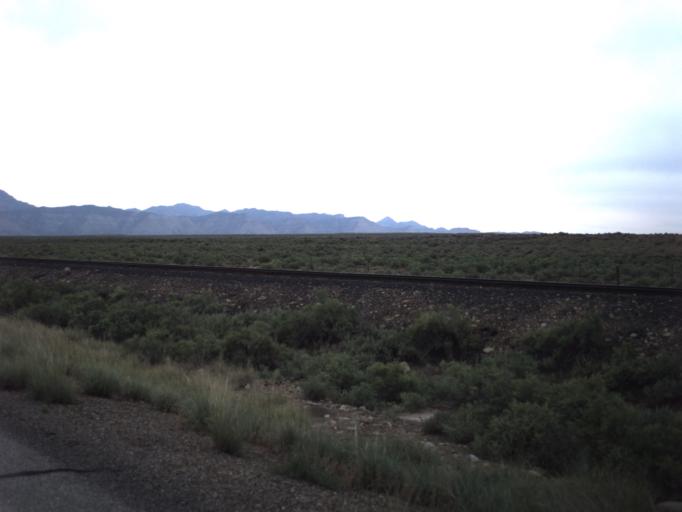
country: US
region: Utah
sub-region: Carbon County
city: East Carbon City
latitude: 39.5316
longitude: -110.5488
